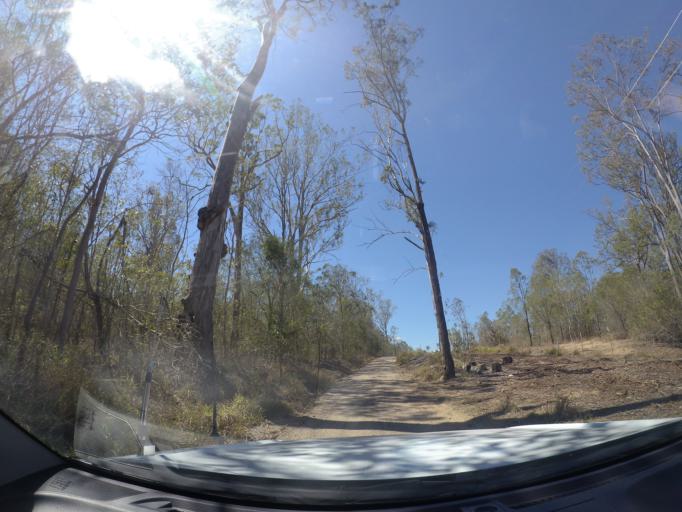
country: AU
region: Queensland
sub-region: Logan
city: North Maclean
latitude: -27.7614
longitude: 152.9416
